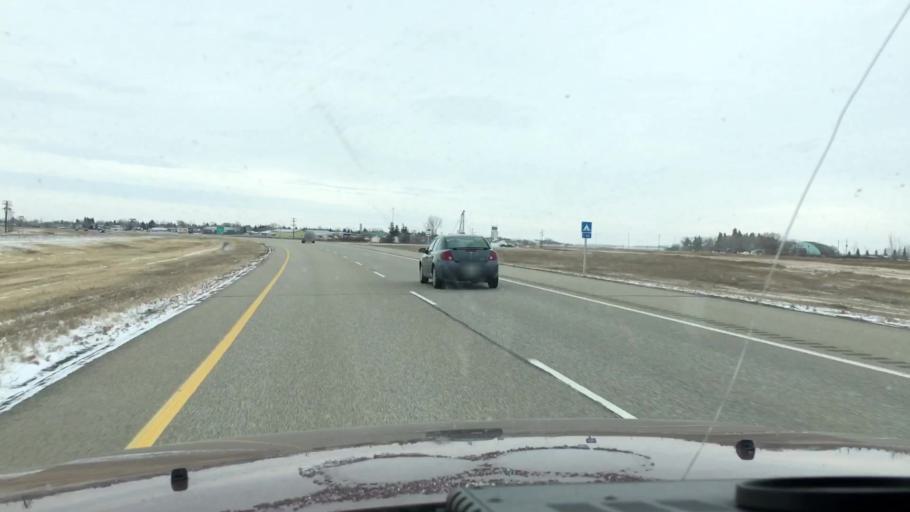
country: CA
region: Saskatchewan
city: Watrous
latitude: 51.2751
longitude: -106.0079
